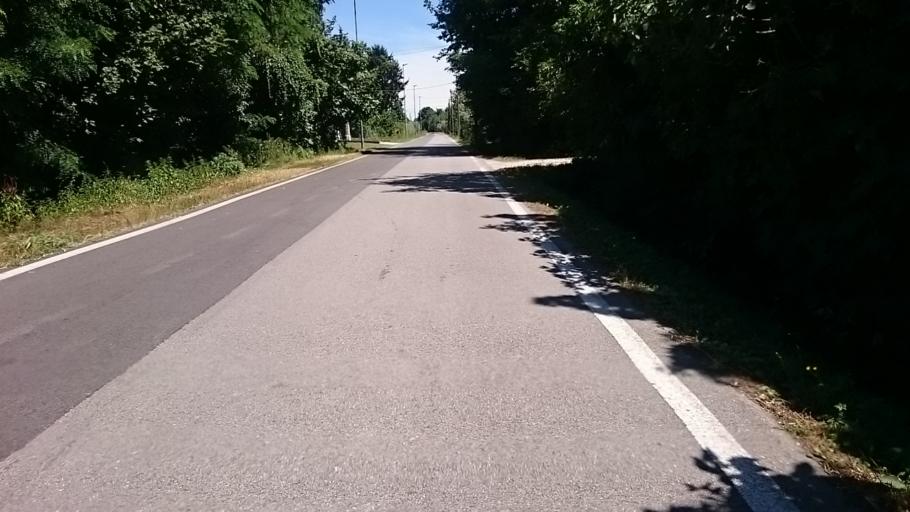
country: IT
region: Veneto
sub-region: Provincia di Padova
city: Borgoricco-San Michele delle Badesse-Sant'Eufemia
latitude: 45.5172
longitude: 11.9473
